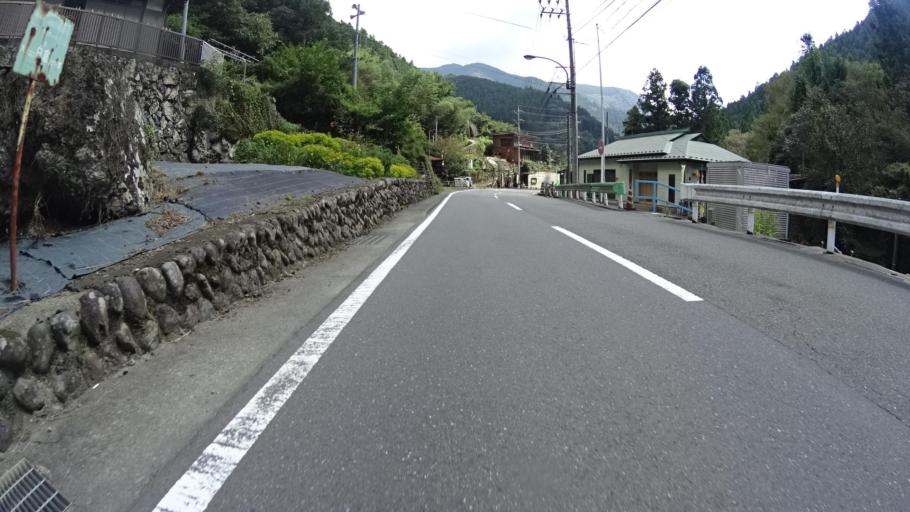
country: JP
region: Tokyo
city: Itsukaichi
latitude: 35.7403
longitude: 139.1338
